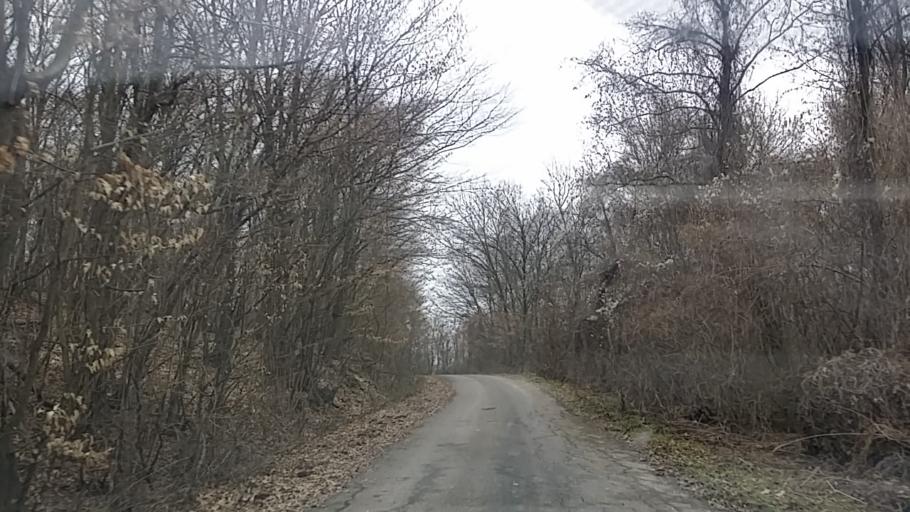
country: HU
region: Borsod-Abauj-Zemplen
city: Rudabanya
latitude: 48.3968
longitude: 20.6504
